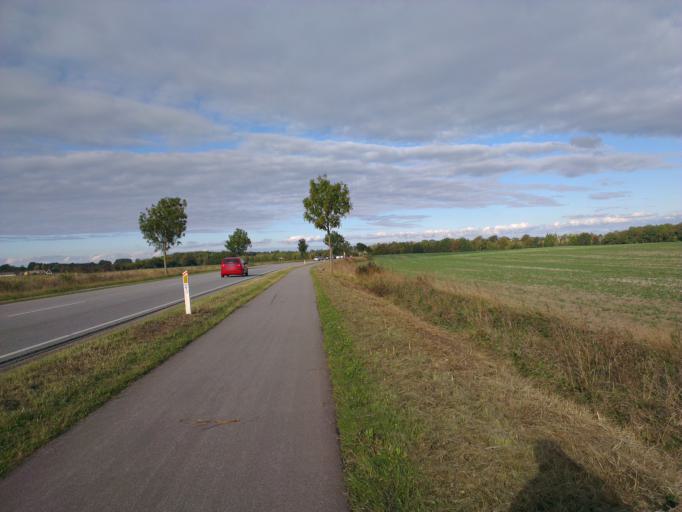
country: DK
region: Capital Region
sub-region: Frederikssund Kommune
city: Skibby
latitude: 55.7312
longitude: 11.9460
